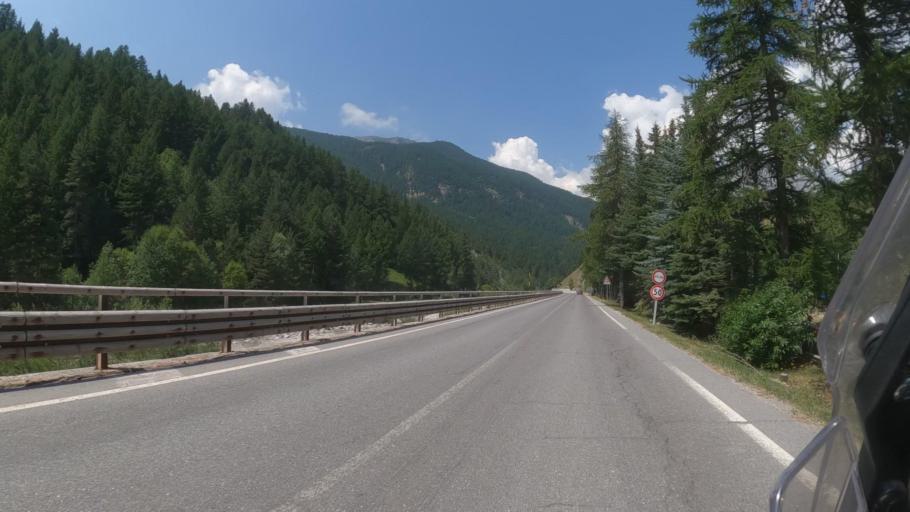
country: IT
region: Piedmont
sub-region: Provincia di Torino
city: Cesana Torinese
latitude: 44.9347
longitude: 6.8148
